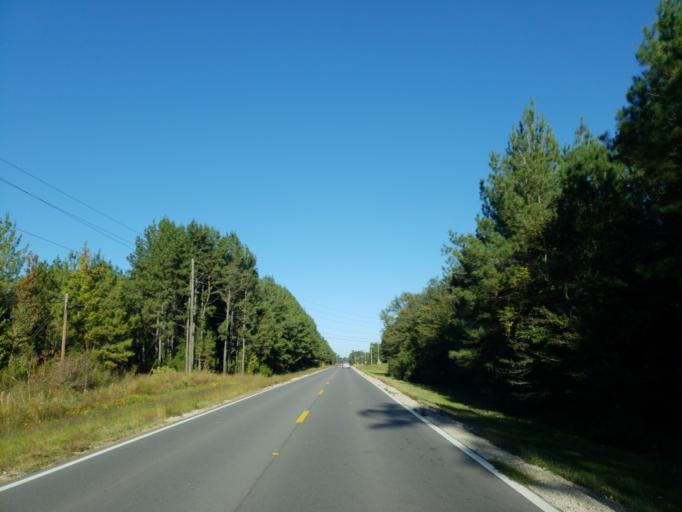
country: US
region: Mississippi
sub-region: Forrest County
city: Petal
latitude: 31.3645
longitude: -89.1430
